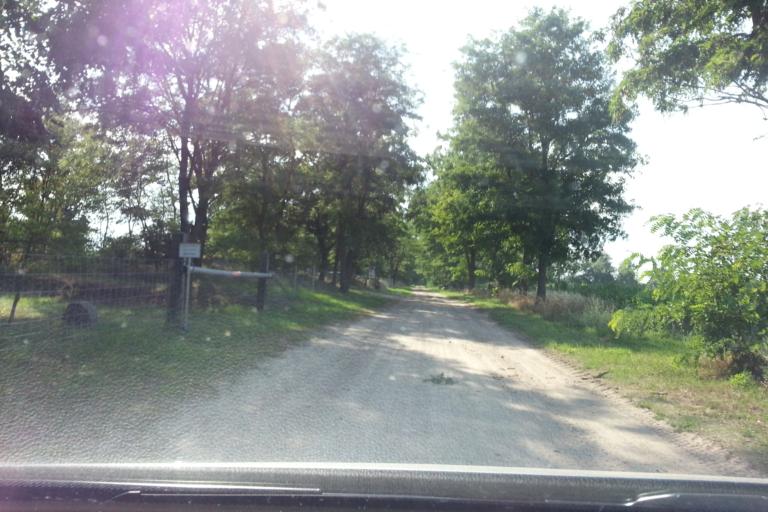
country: DE
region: Mecklenburg-Vorpommern
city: Ferdinandshof
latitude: 53.6429
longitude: 13.8401
